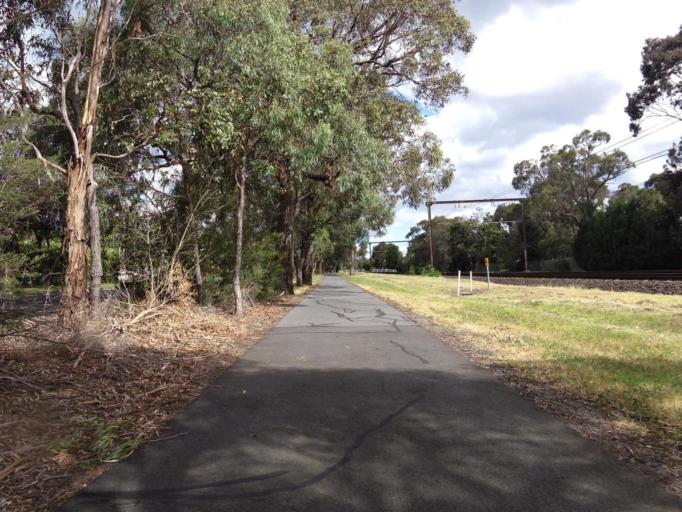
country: AU
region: Victoria
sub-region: Knox
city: Bayswater
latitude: -37.8523
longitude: 145.2786
